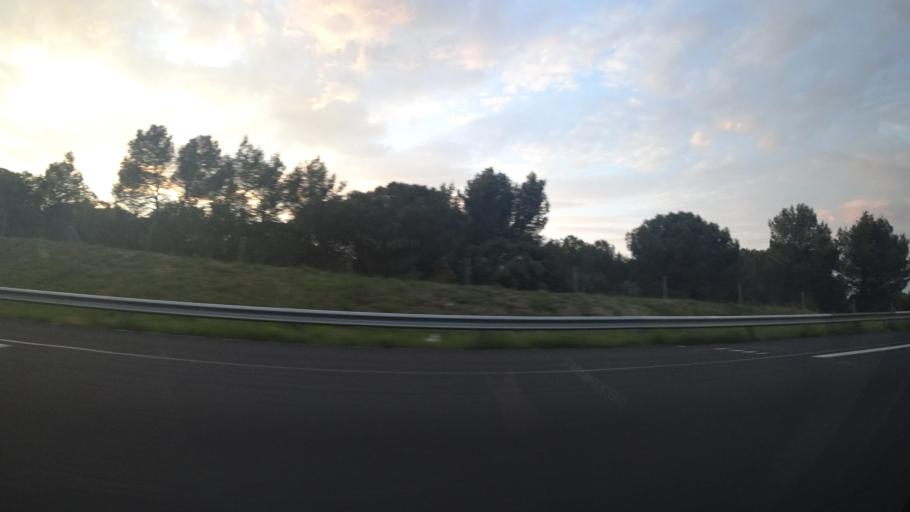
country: FR
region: Languedoc-Roussillon
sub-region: Departement de l'Aude
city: Fleury
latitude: 43.2279
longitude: 3.1041
